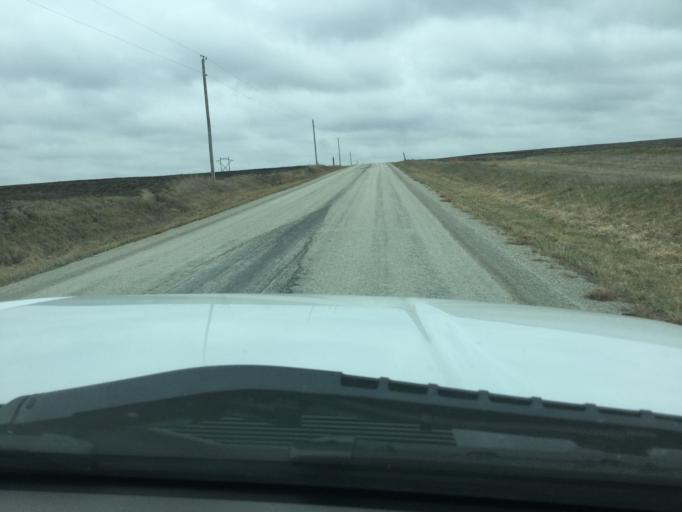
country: US
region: Kansas
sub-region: Nemaha County
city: Sabetha
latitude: 39.7981
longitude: -95.7835
